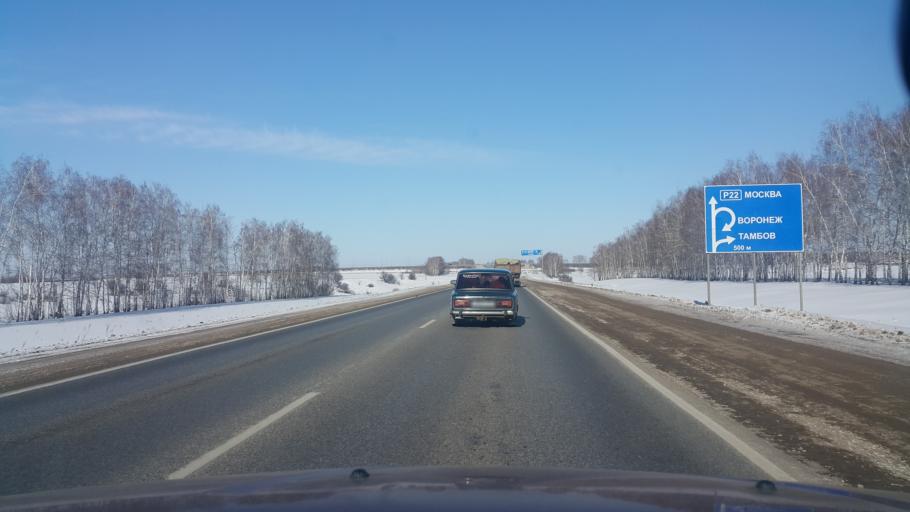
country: RU
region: Tambov
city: Pokrovo-Prigorodnoye
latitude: 52.6532
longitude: 41.3404
